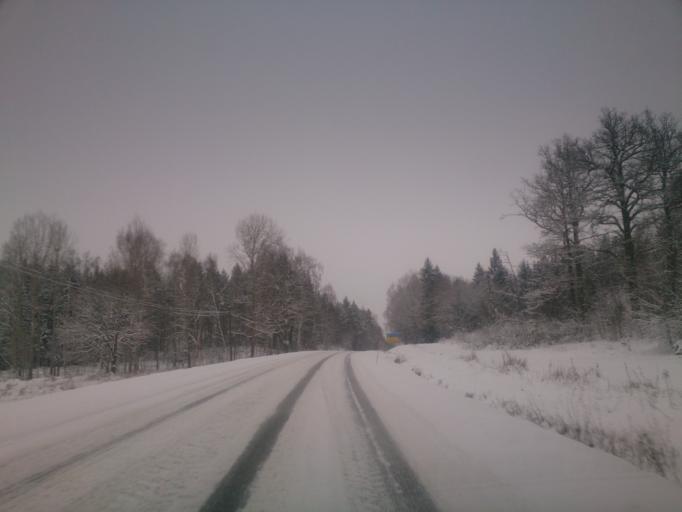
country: SE
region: OEstergoetland
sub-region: Finspangs Kommun
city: Finspang
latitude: 58.6330
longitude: 15.8210
